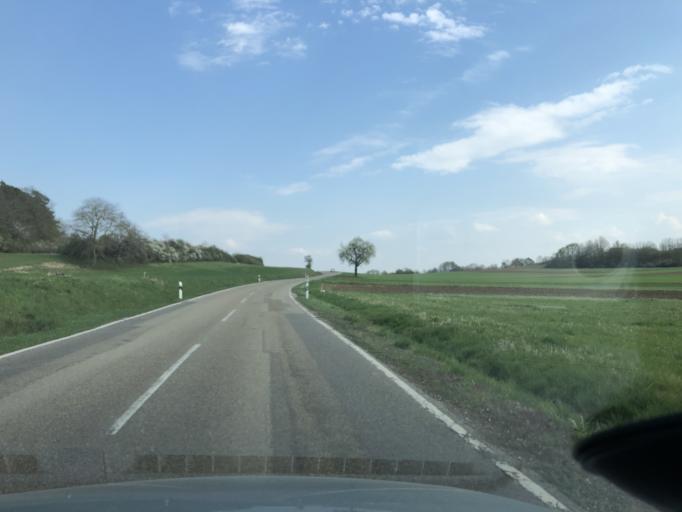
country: DE
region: Baden-Wuerttemberg
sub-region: Karlsruhe Region
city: Simmozheim
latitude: 48.7626
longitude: 8.8059
